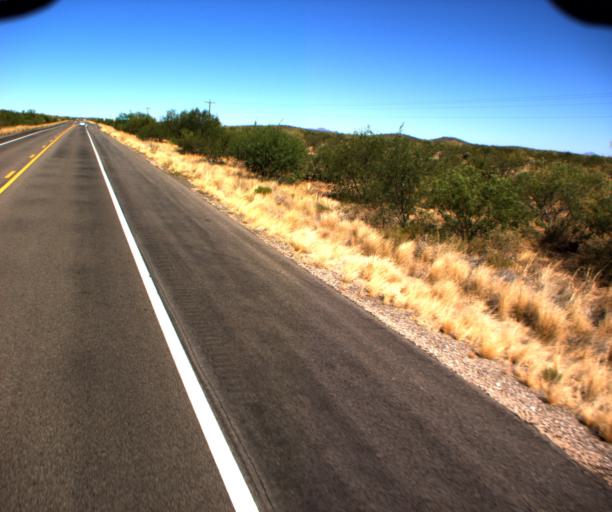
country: US
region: Arizona
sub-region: Pima County
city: Three Points
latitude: 32.0400
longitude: -111.4789
